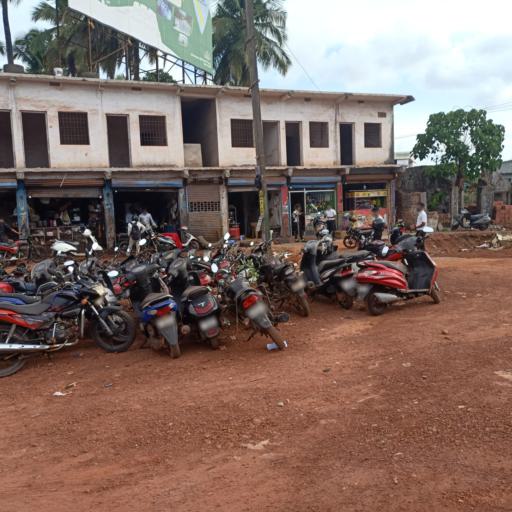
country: IN
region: Kerala
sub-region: Kasaragod District
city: Kasaragod
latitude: 12.5094
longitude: 75.0535
